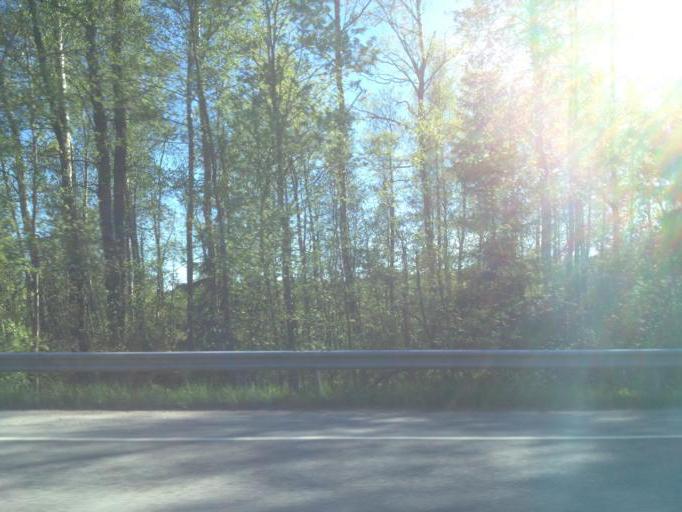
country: FI
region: Uusimaa
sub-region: Helsinki
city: Espoo
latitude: 60.2416
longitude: 24.5878
